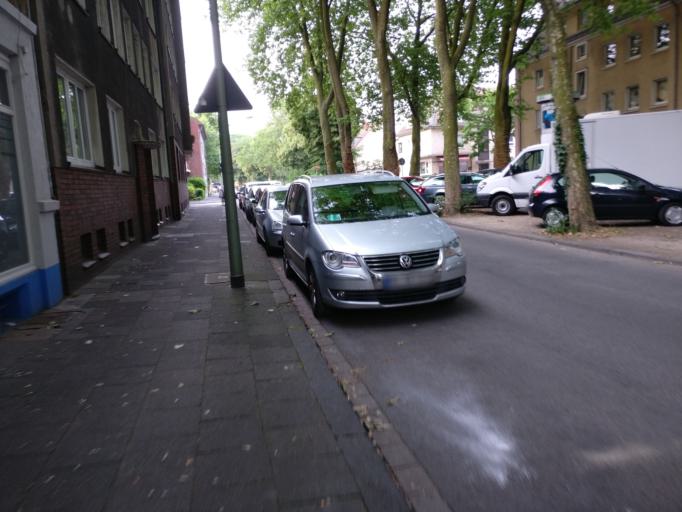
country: DE
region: North Rhine-Westphalia
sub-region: Regierungsbezirk Dusseldorf
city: Duisburg
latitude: 51.4264
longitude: 6.7936
